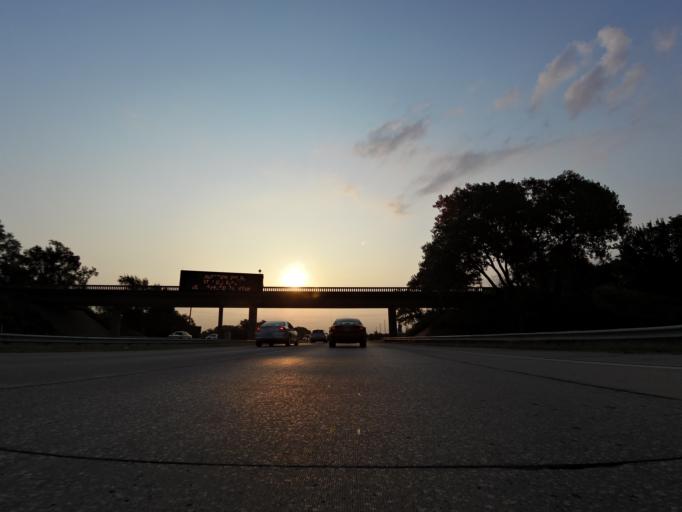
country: US
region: Kansas
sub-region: Sedgwick County
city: Park City
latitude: 37.7568
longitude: -97.3547
